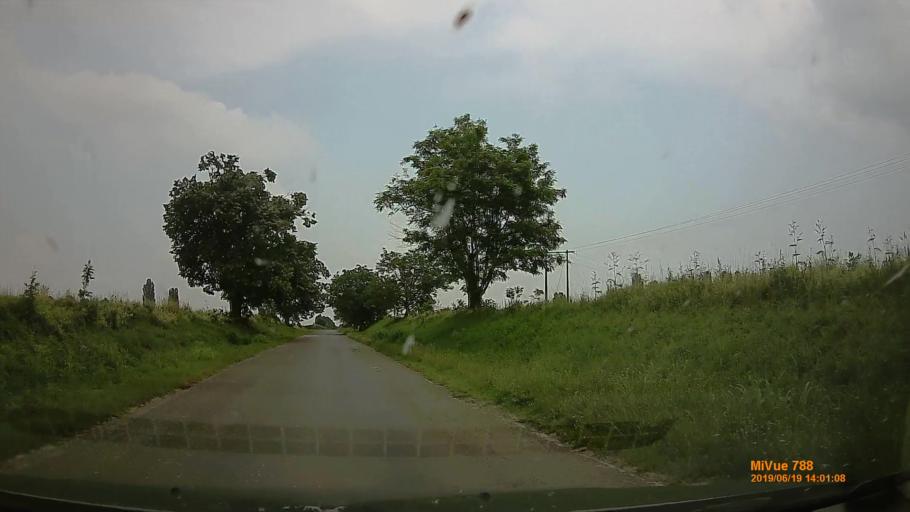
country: HU
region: Baranya
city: Szigetvar
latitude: 46.0822
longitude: 17.8135
